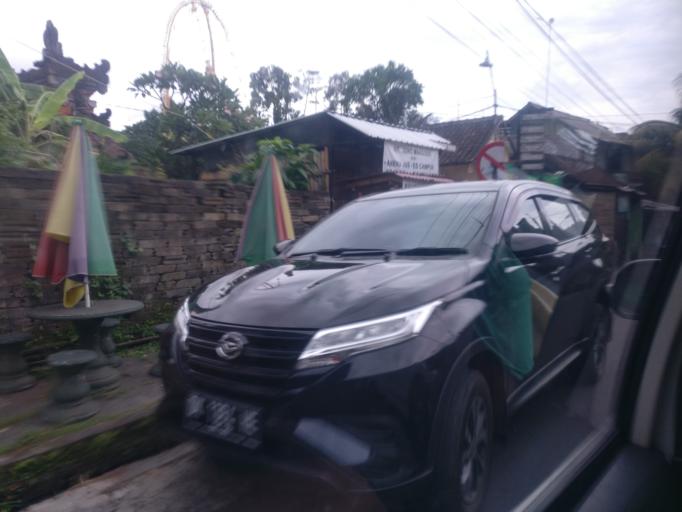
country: ID
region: Bali
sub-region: Kabupaten Gianyar
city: Ubud
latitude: -8.5163
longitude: 115.2652
